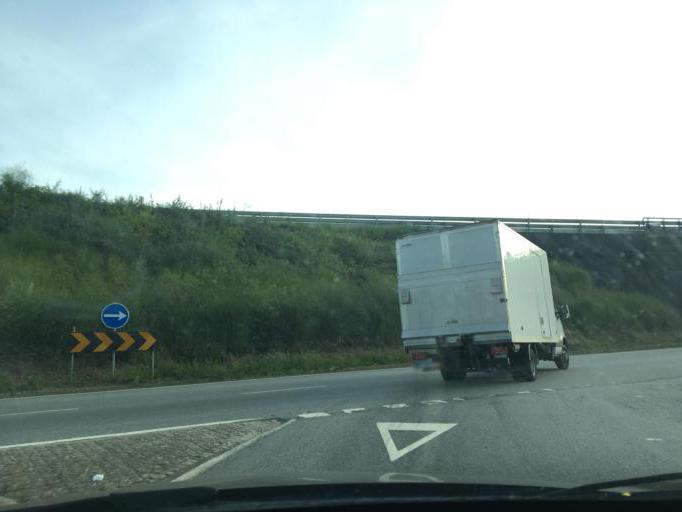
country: PT
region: Porto
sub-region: Maia
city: Maia
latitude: 41.2413
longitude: -8.6275
